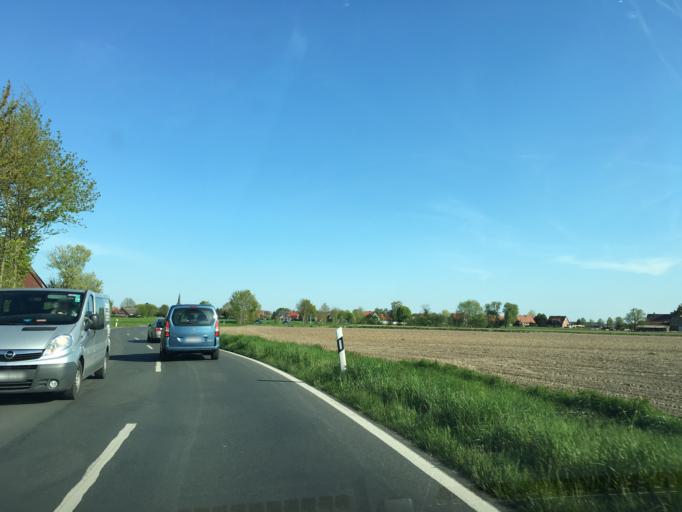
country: DE
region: North Rhine-Westphalia
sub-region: Regierungsbezirk Munster
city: Senden
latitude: 51.8288
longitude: 7.5263
